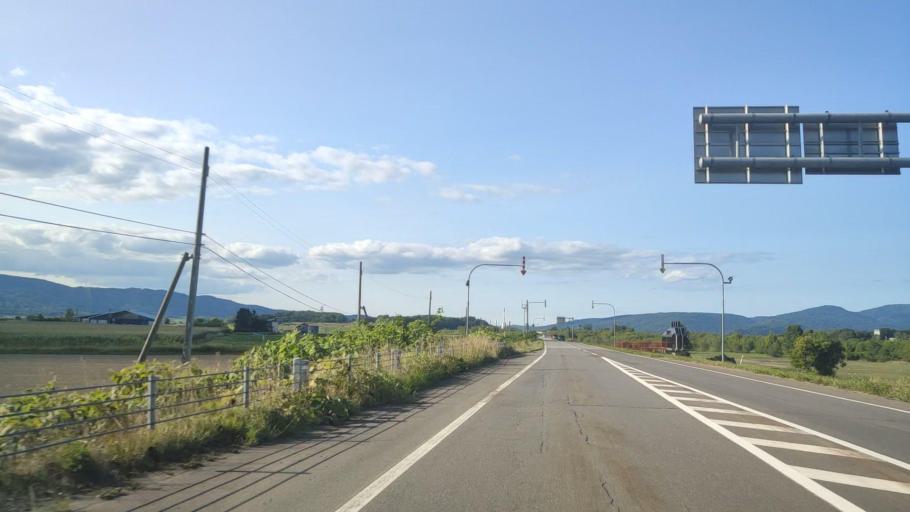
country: JP
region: Hokkaido
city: Nayoro
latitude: 44.8038
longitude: 142.0674
